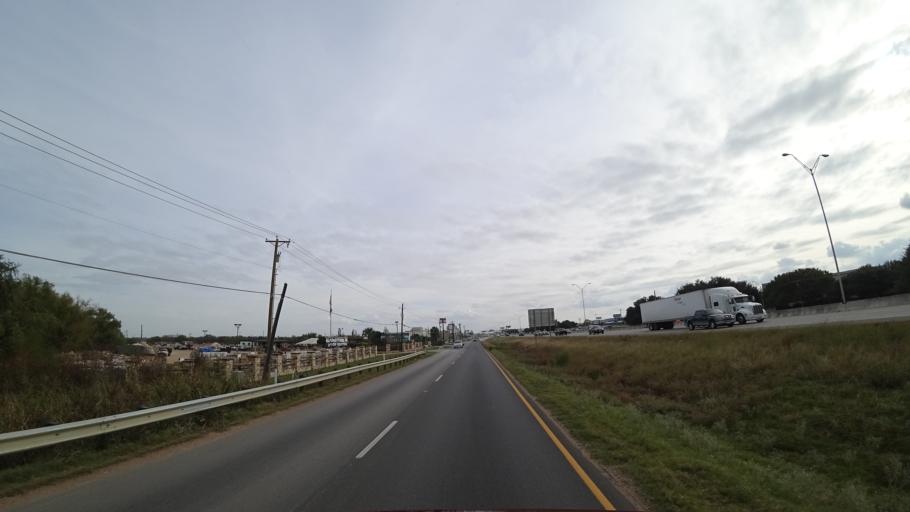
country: US
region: Texas
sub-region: Travis County
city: Windemere
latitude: 30.4751
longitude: -97.6719
